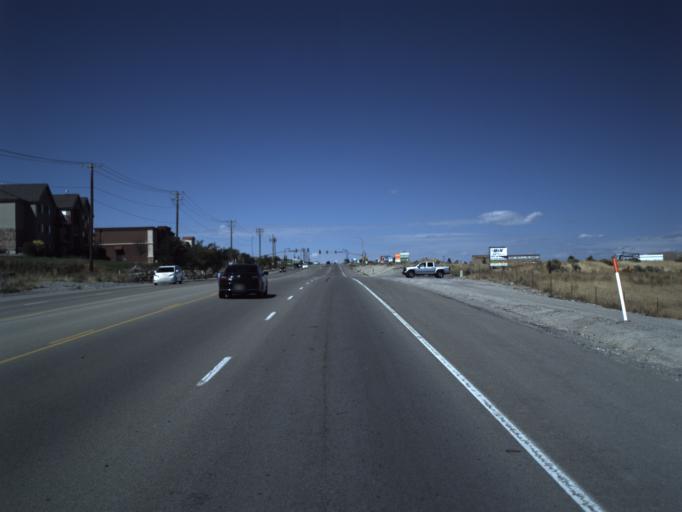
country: US
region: Utah
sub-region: Utah County
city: Saratoga Springs
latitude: 40.3960
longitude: -111.9182
